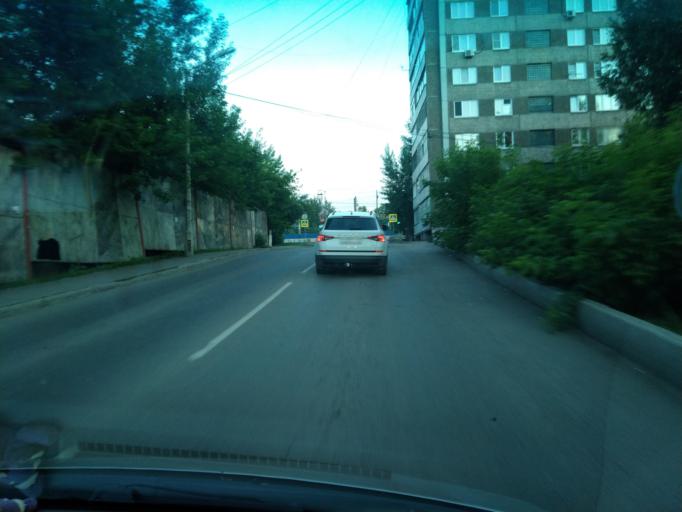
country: RU
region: Krasnoyarskiy
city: Krasnoyarsk
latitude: 55.9840
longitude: 92.8716
